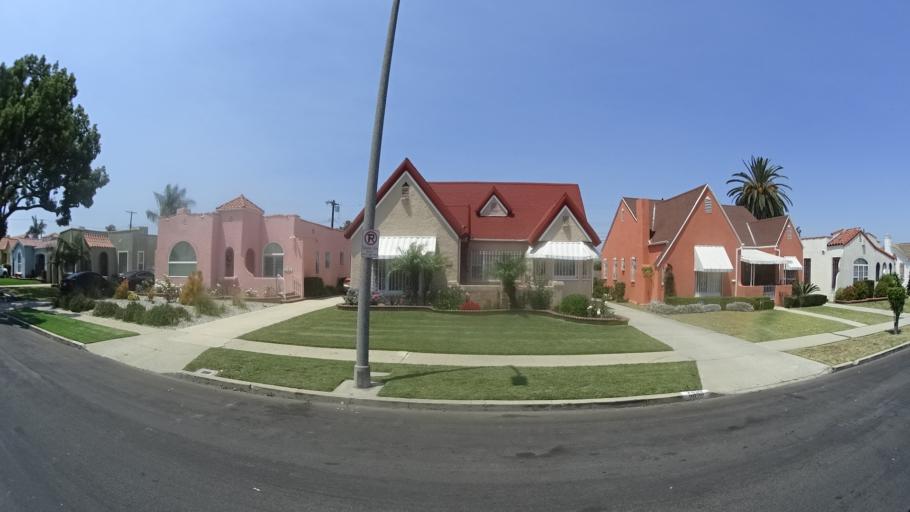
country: US
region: California
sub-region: Los Angeles County
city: Westmont
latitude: 33.9664
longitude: -118.3146
